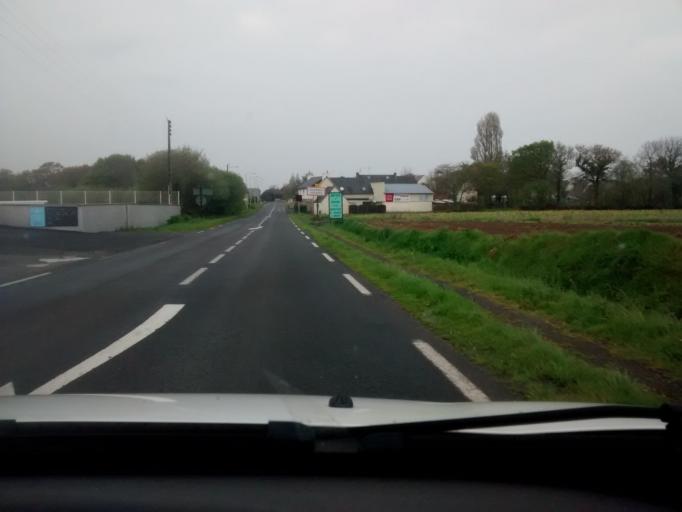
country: FR
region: Brittany
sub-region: Departement des Cotes-d'Armor
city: Louannec
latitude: 48.7910
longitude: -3.4033
